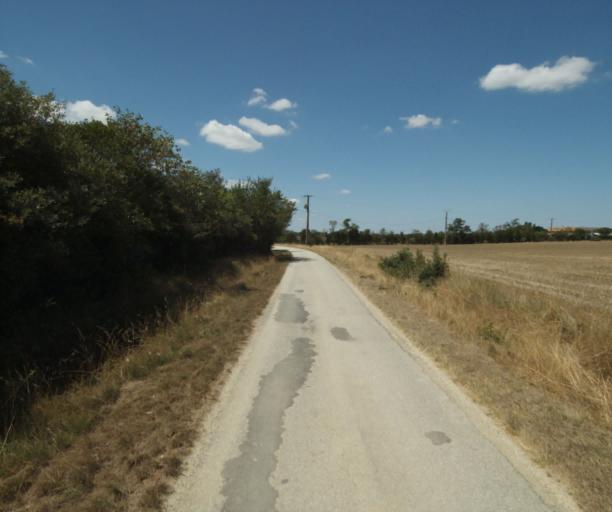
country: FR
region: Midi-Pyrenees
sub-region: Departement de la Haute-Garonne
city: Auriac-sur-Vendinelle
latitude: 43.4987
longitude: 1.8511
